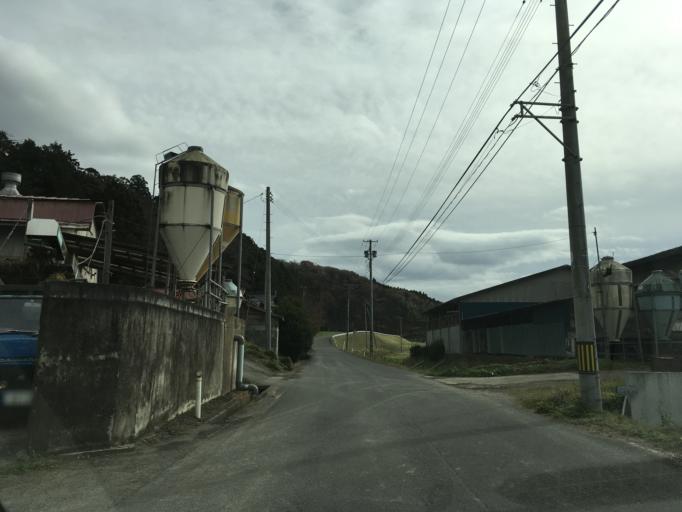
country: JP
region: Iwate
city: Ichinoseki
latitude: 38.7686
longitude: 141.2720
